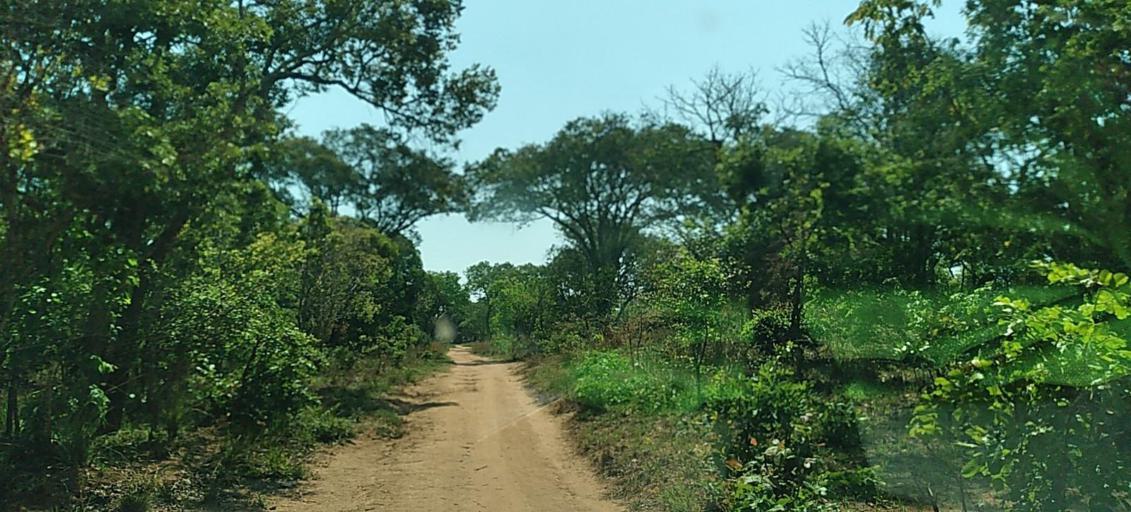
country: CD
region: Katanga
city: Kolwezi
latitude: -11.2790
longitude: 25.1318
